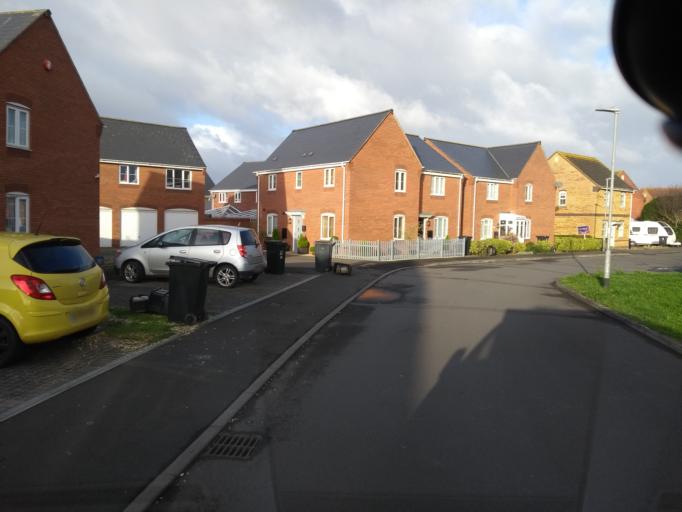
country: GB
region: England
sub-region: Somerset
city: Highbridge
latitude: 51.2315
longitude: -2.9801
